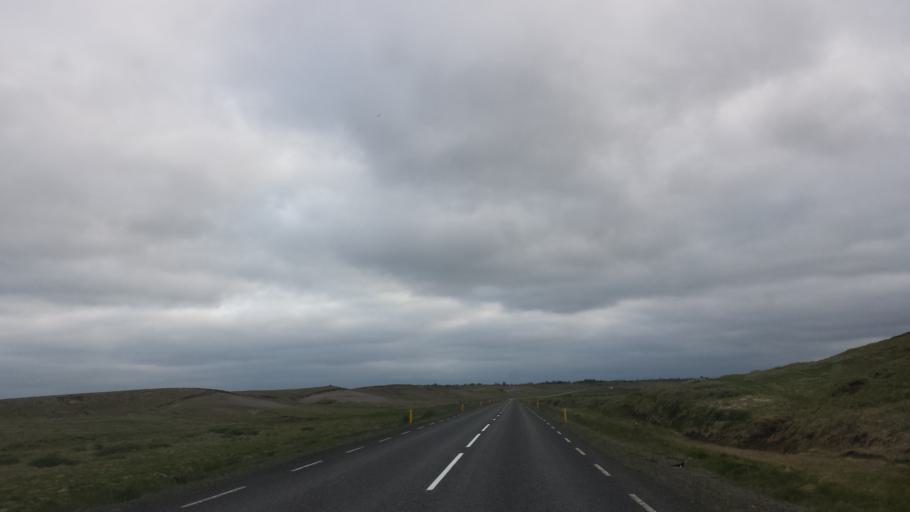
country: IS
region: South
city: Selfoss
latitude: 64.1288
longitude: -20.5866
